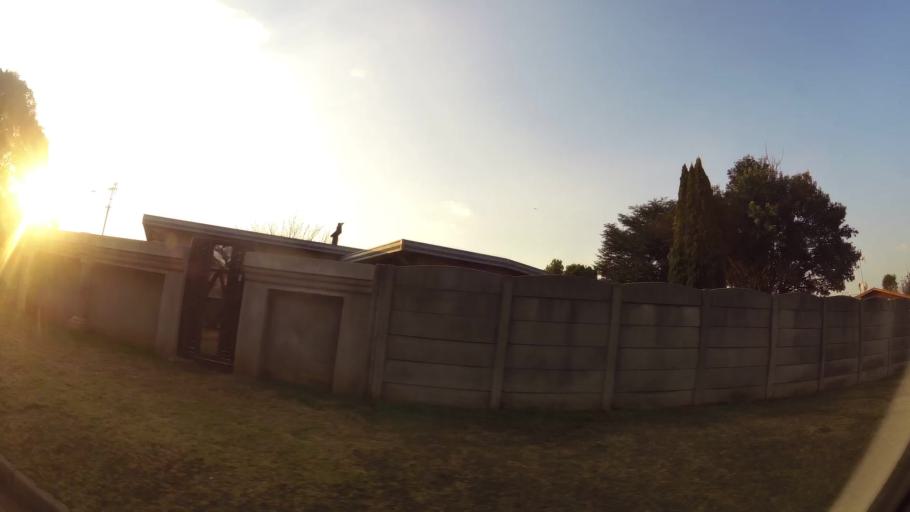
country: ZA
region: Gauteng
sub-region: Ekurhuleni Metropolitan Municipality
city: Springs
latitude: -26.2665
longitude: 28.4075
